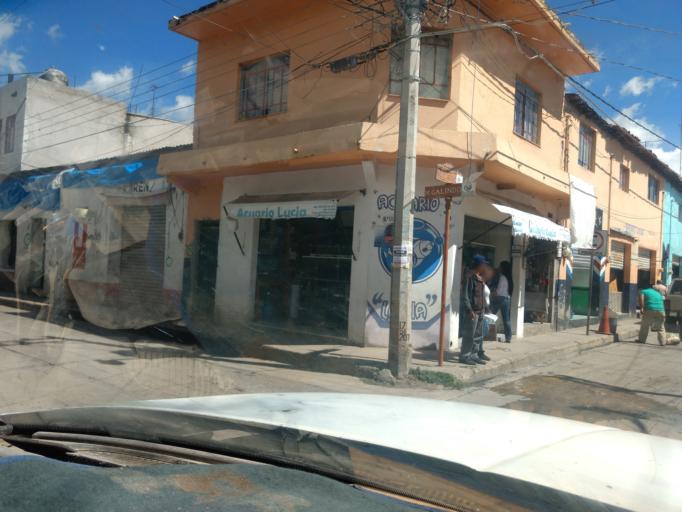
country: MX
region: Oaxaca
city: Ciudad de Huajuapam de Leon
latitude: 17.8054
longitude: -97.7768
